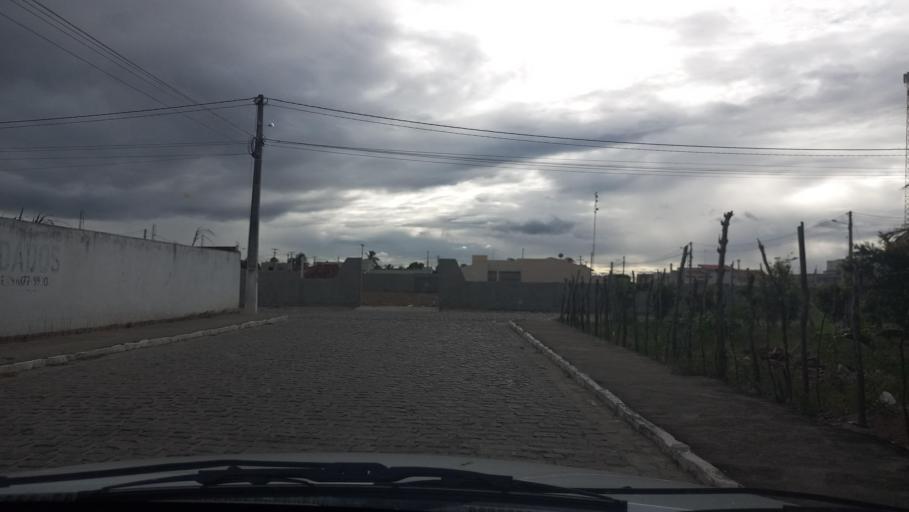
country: BR
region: Rio Grande do Norte
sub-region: Brejinho
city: Brejinho
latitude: -6.0493
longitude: -35.4338
